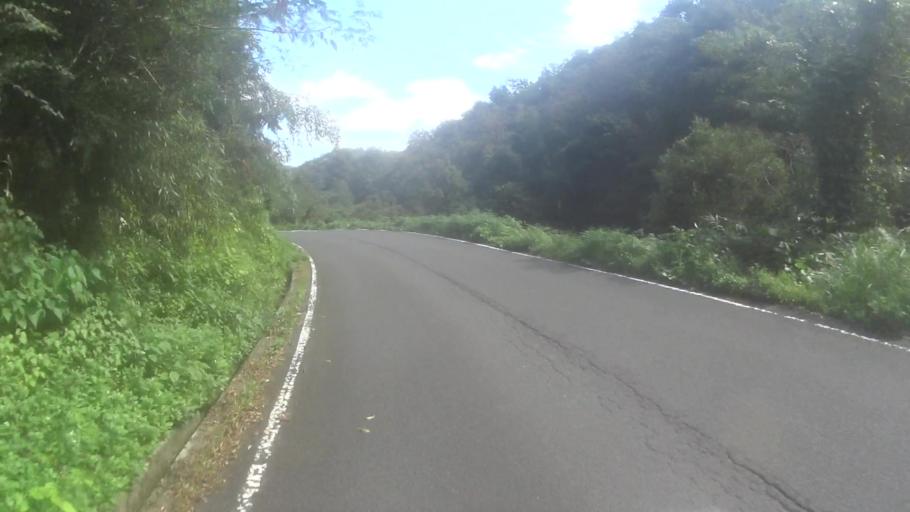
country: JP
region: Kyoto
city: Miyazu
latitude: 35.6112
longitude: 135.1139
